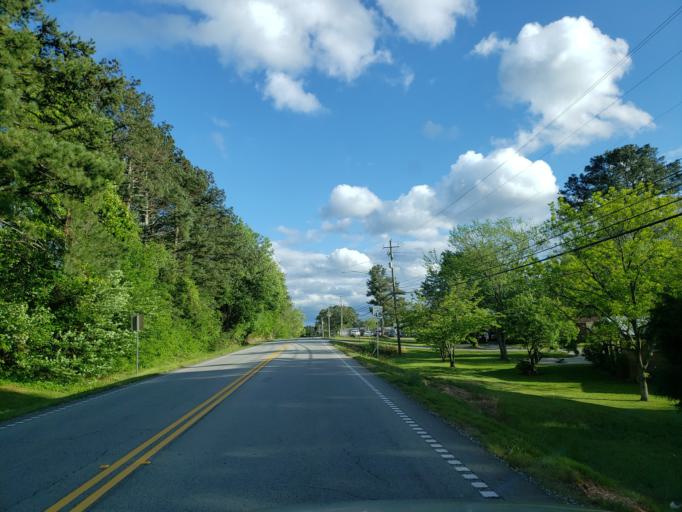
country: US
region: Georgia
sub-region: Haralson County
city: Tallapoosa
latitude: 33.7629
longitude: -85.2944
